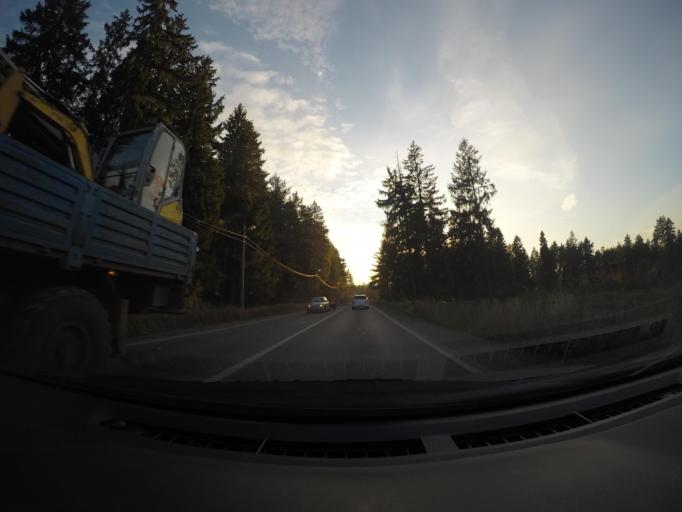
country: RU
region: Moskovskaya
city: Firsanovka
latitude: 55.9642
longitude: 37.2556
